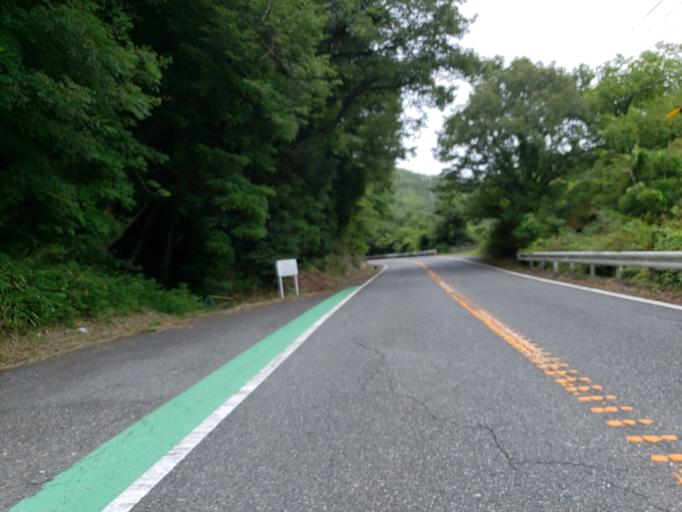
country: JP
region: Hyogo
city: Aioi
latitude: 34.7675
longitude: 134.4740
